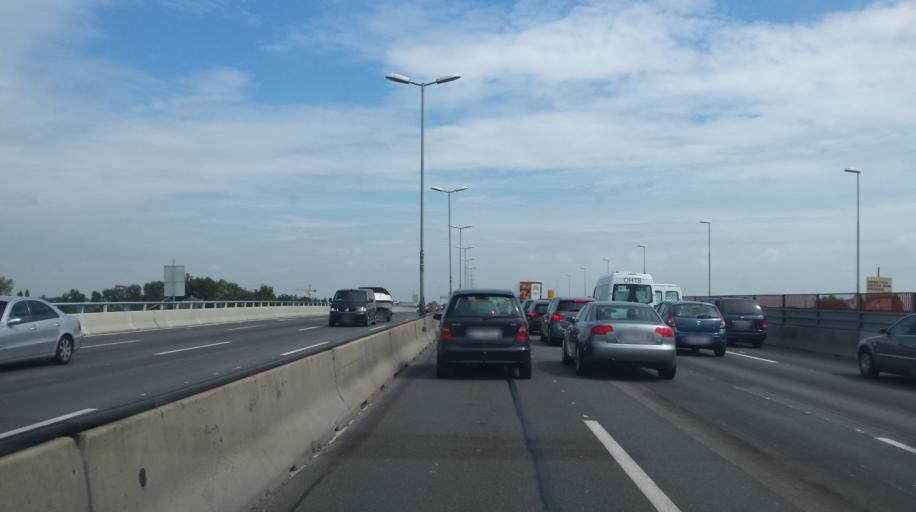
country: AT
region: Vienna
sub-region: Wien Stadt
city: Vienna
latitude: 48.2058
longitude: 16.4357
